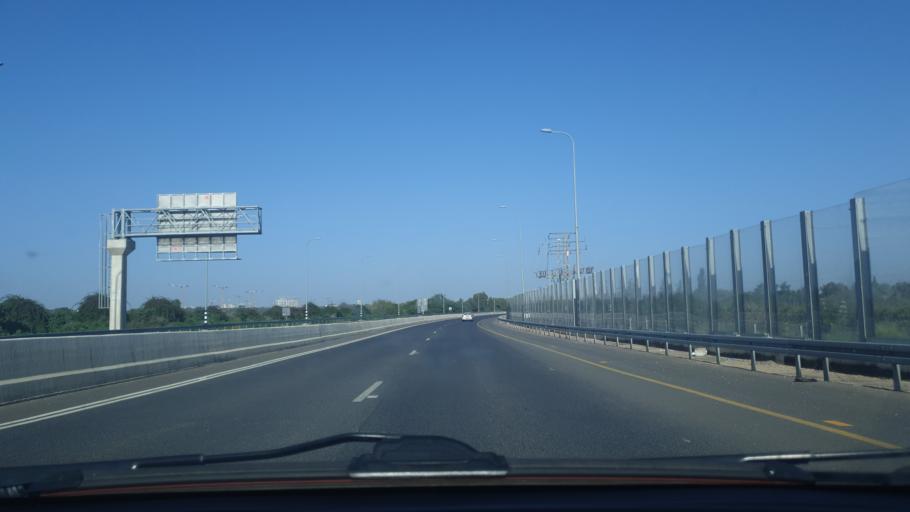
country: IL
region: Central District
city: Ramla
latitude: 31.9454
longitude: 34.8608
